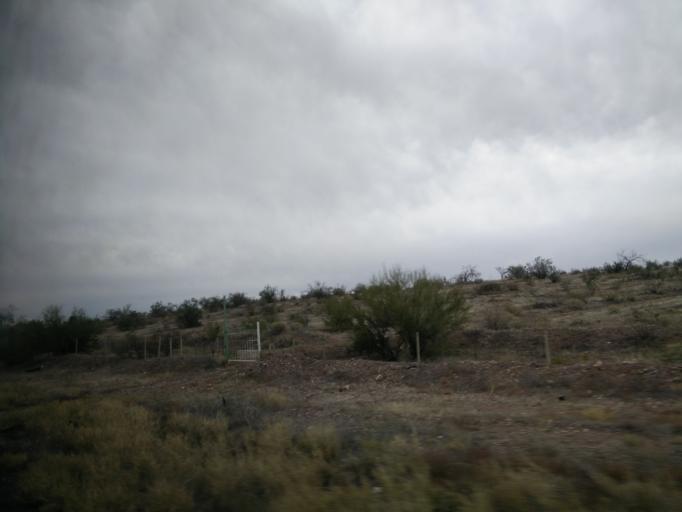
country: MX
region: Sonora
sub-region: Hermosillo
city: Miguel Aleman (La Doce)
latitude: 28.5036
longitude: -111.0453
